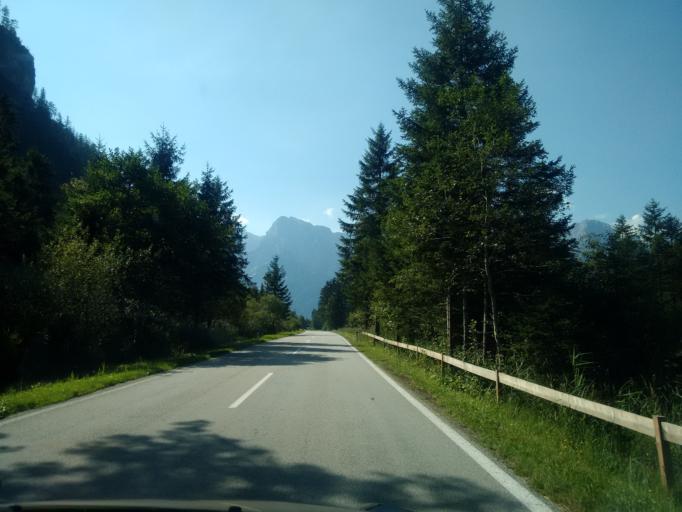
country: AT
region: Upper Austria
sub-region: Politischer Bezirk Gmunden
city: Gruenau im Almtal
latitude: 47.7718
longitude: 13.9571
